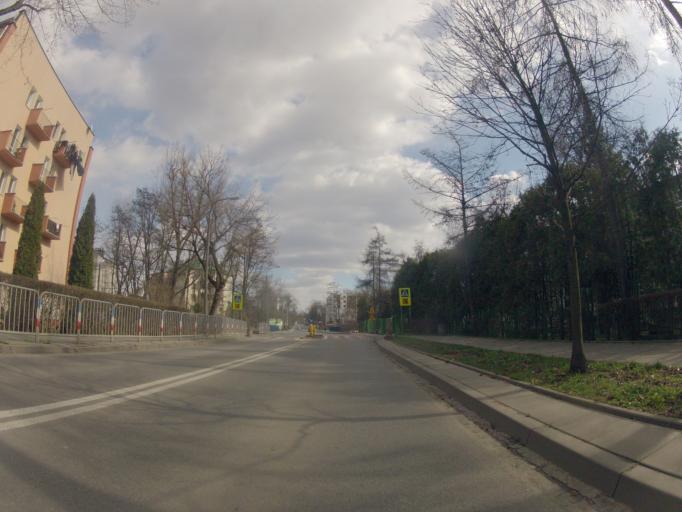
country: PL
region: Lesser Poland Voivodeship
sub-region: Krakow
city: Krakow
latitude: 50.0812
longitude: 19.9556
